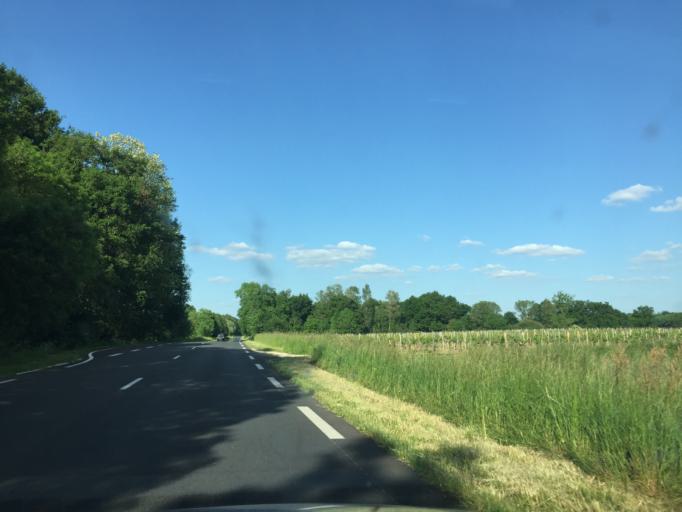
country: FR
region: Aquitaine
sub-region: Departement de la Gironde
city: Saint-Denis-de-Pile
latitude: 45.0019
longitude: -0.1846
